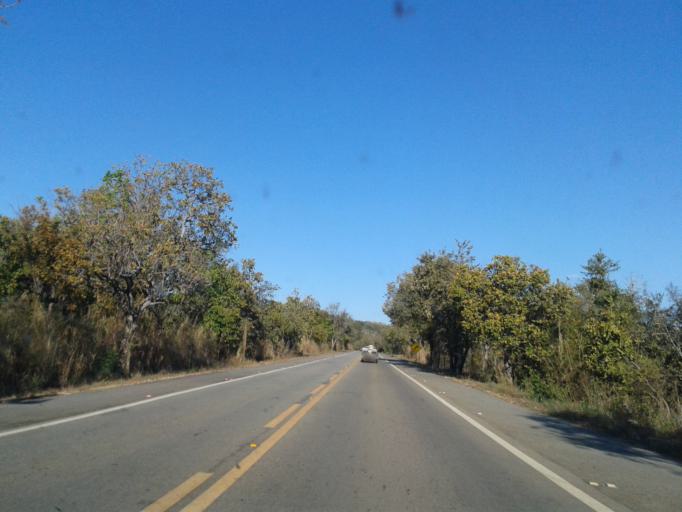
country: BR
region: Goias
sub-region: Itapuranga
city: Itapuranga
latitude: -15.3589
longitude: -50.3974
